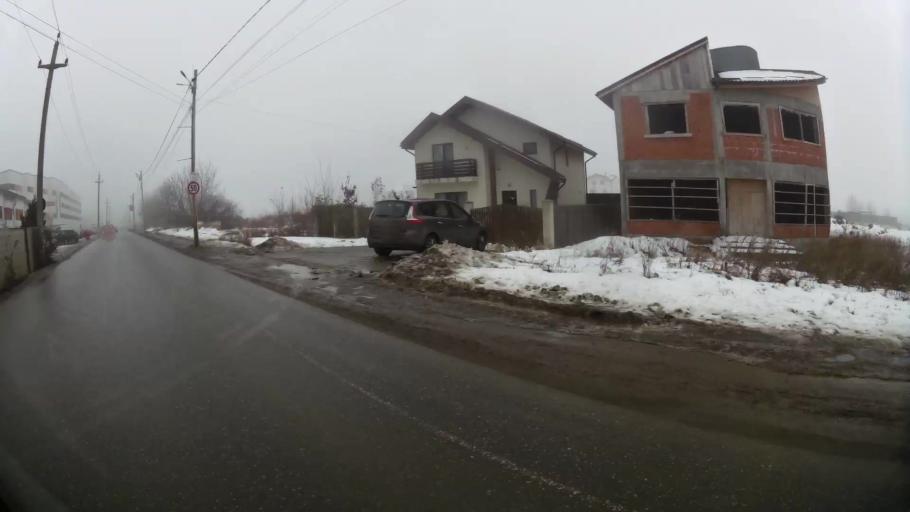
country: RO
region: Ilfov
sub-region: Comuna Chiajna
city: Chiajna
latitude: 44.4509
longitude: 25.9767
